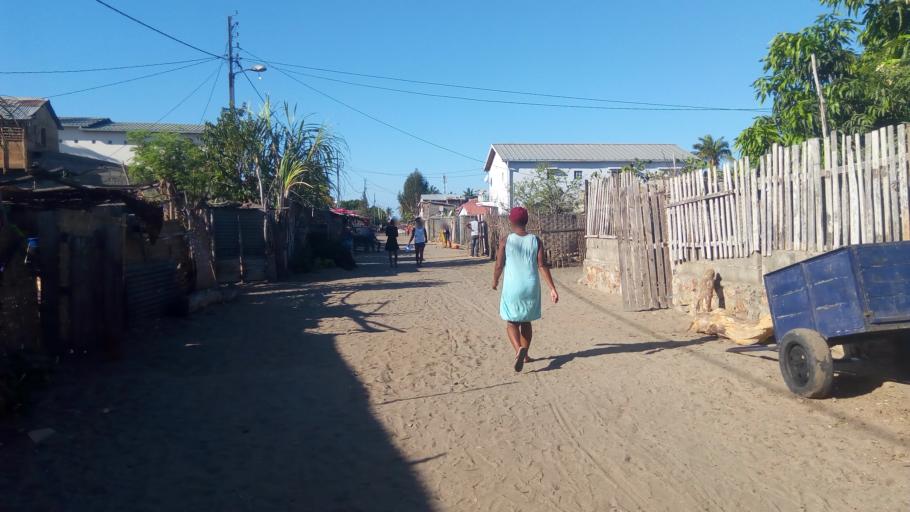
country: MG
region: Menabe
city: Morondava
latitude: -20.2988
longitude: 44.2793
